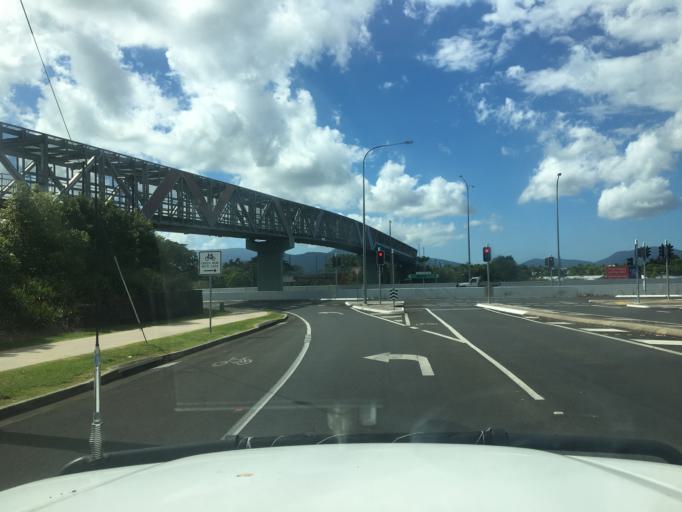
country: AU
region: Queensland
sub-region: Cairns
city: Woree
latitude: -16.9677
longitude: 145.7458
